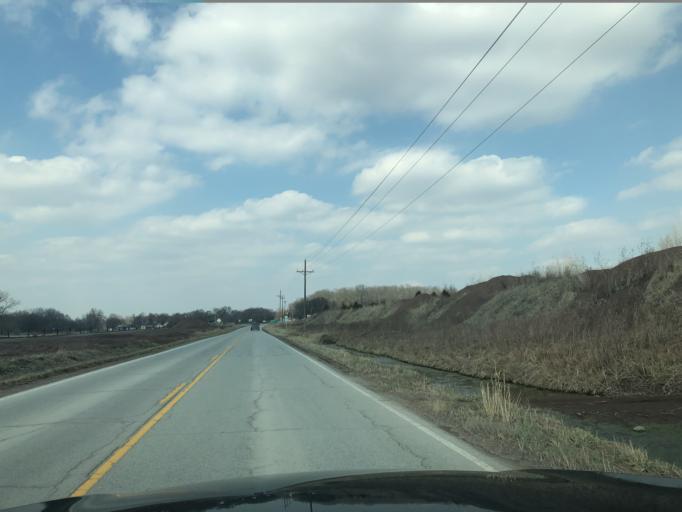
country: US
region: Missouri
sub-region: Platte County
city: Platte City
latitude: 39.4946
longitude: -94.8026
